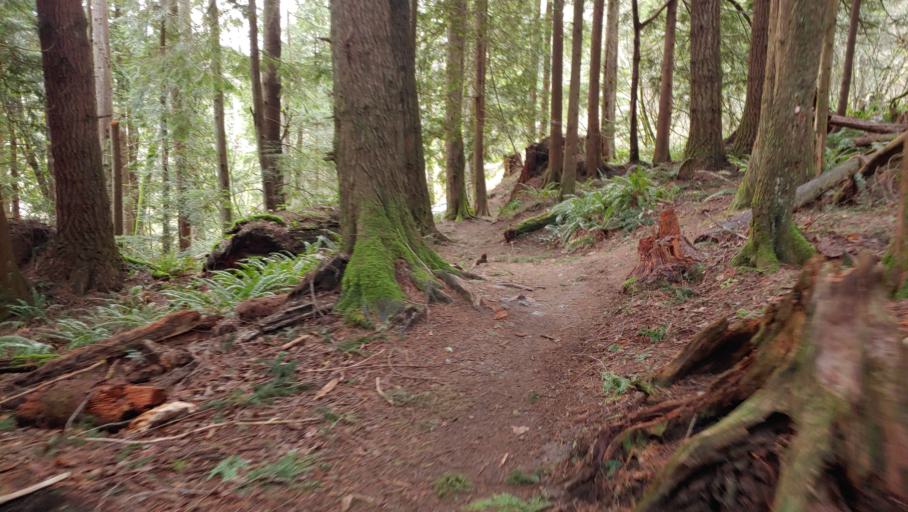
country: US
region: Washington
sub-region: King County
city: Hobart
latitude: 47.4705
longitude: -121.9210
